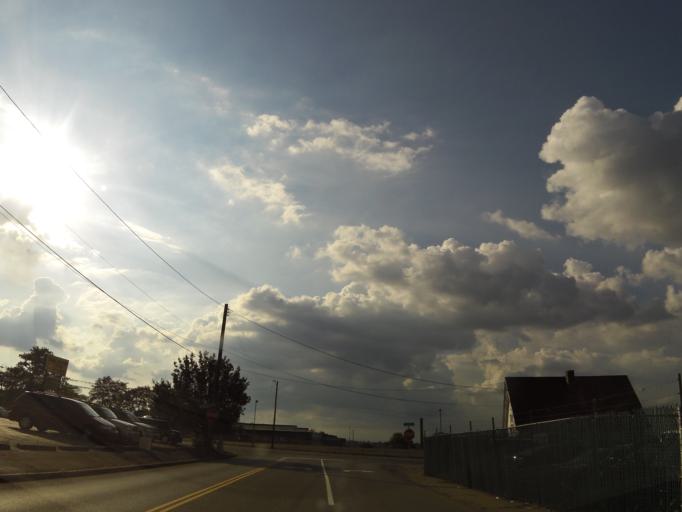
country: US
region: Tennessee
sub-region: Montgomery County
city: Clarksville
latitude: 36.5349
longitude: -87.3401
